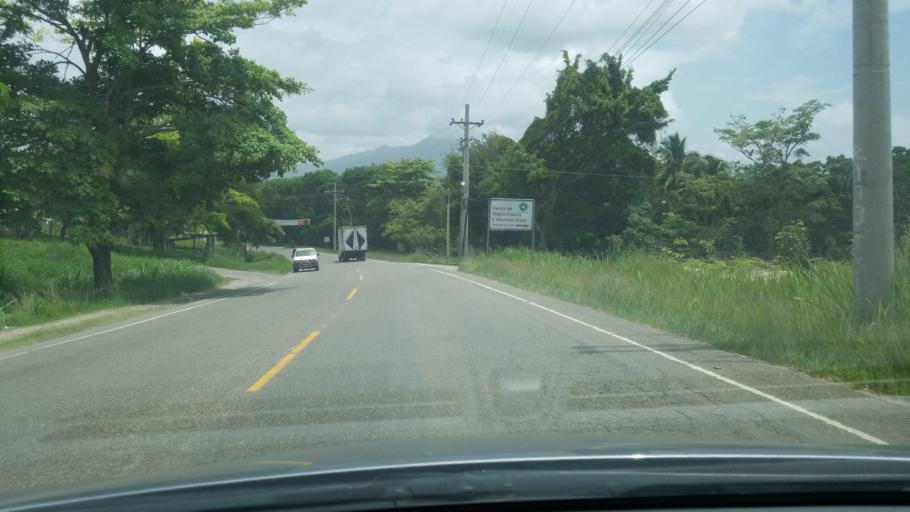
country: HN
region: Copan
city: Cucuyagua
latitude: 14.6691
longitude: -88.8633
